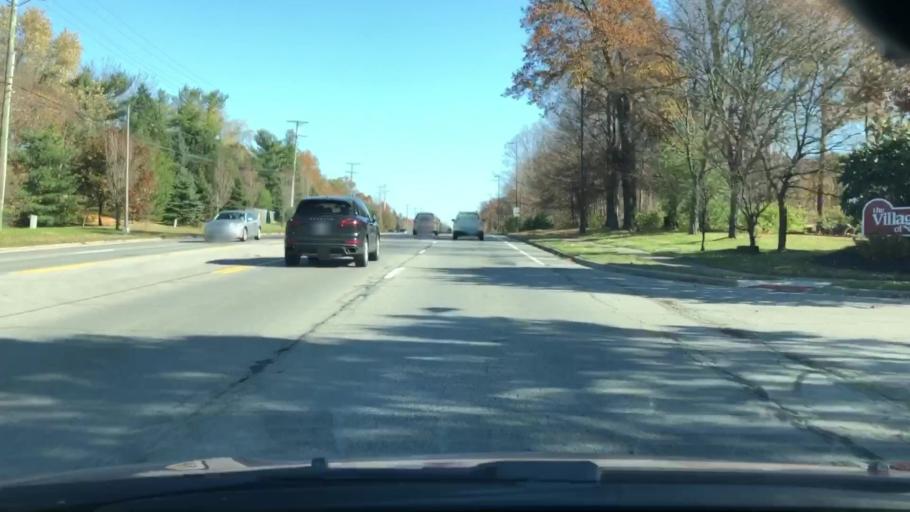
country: US
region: Ohio
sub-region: Franklin County
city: Gahanna
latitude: 40.0560
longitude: -82.8820
